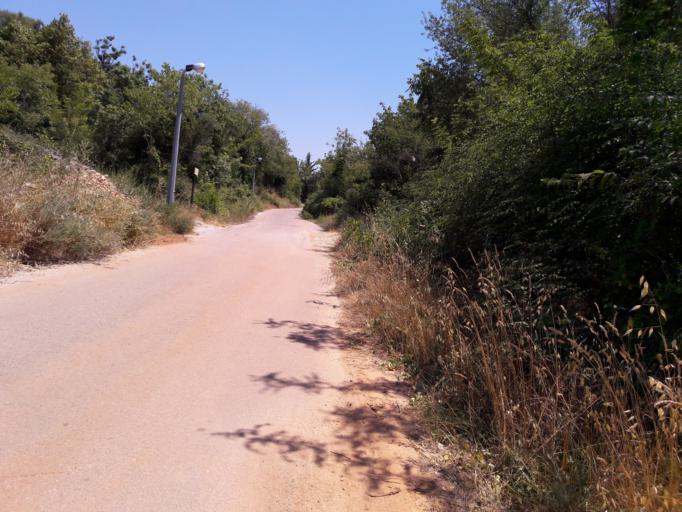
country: HR
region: Sibensko-Kniniska
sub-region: Grad Sibenik
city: Sibenik
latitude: 43.6945
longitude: 15.8393
